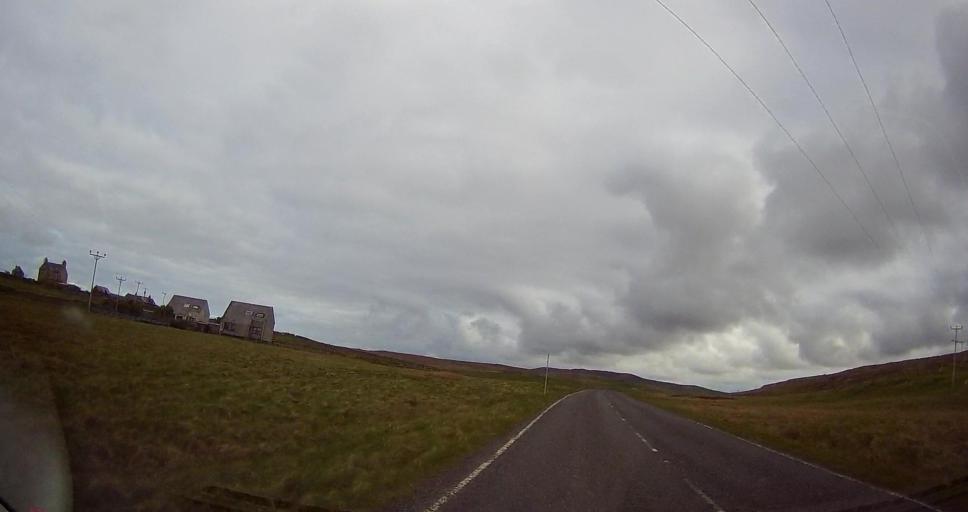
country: GB
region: Scotland
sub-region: Shetland Islands
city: Shetland
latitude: 60.6854
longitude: -0.9649
